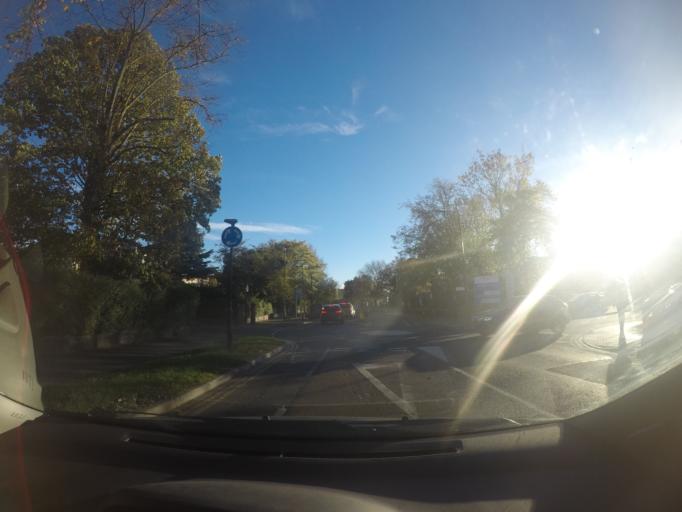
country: GB
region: England
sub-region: City of York
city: York
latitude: 53.9716
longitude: -1.0820
